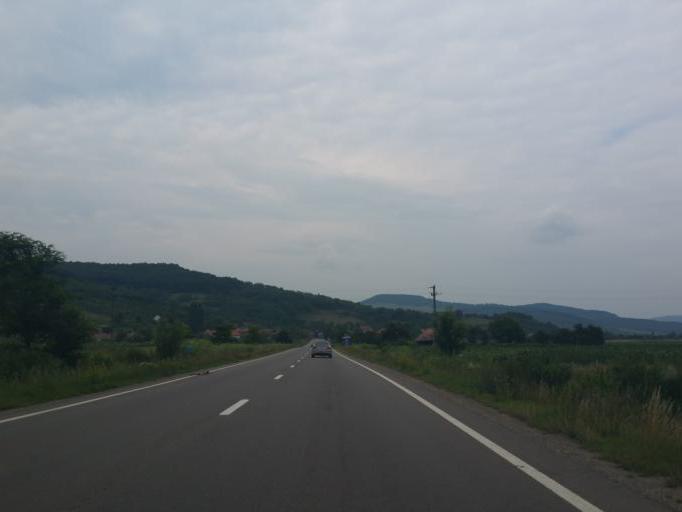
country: RO
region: Salaj
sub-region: Comuna Zimbor
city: Zimbor
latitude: 47.0195
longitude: 23.2633
